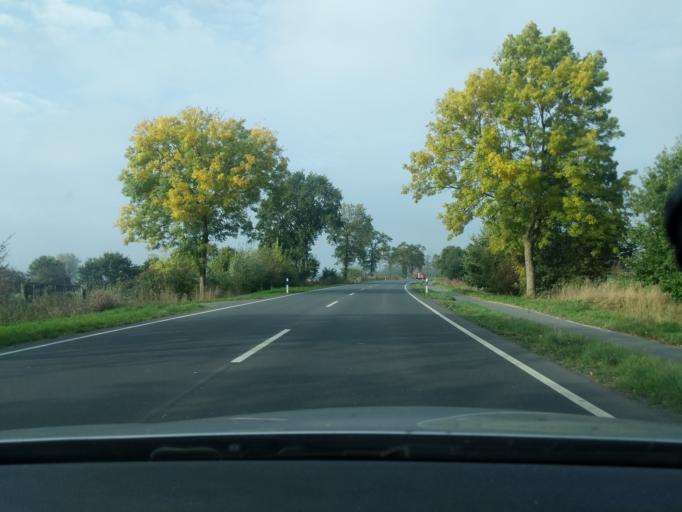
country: DE
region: Lower Saxony
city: Neuhaus an der Oste
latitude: 53.8017
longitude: 9.0256
